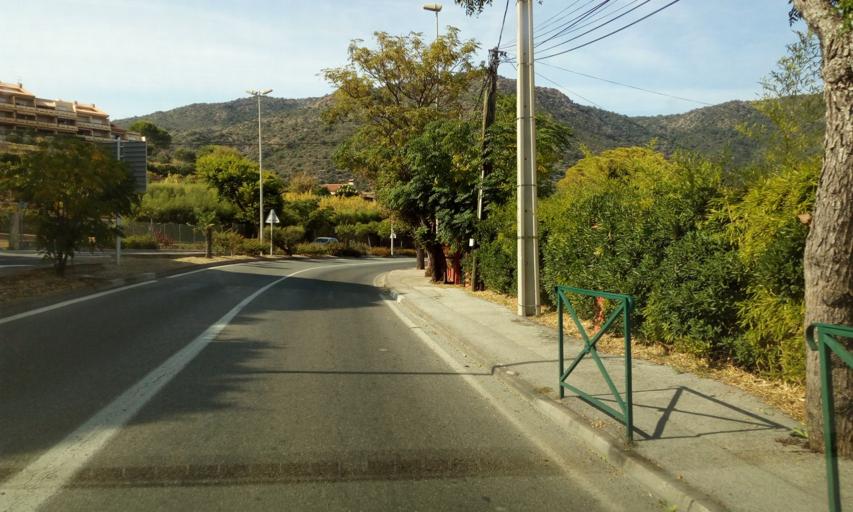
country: FR
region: Provence-Alpes-Cote d'Azur
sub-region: Departement du Var
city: Le Lavandou
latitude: 43.1417
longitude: 6.3795
